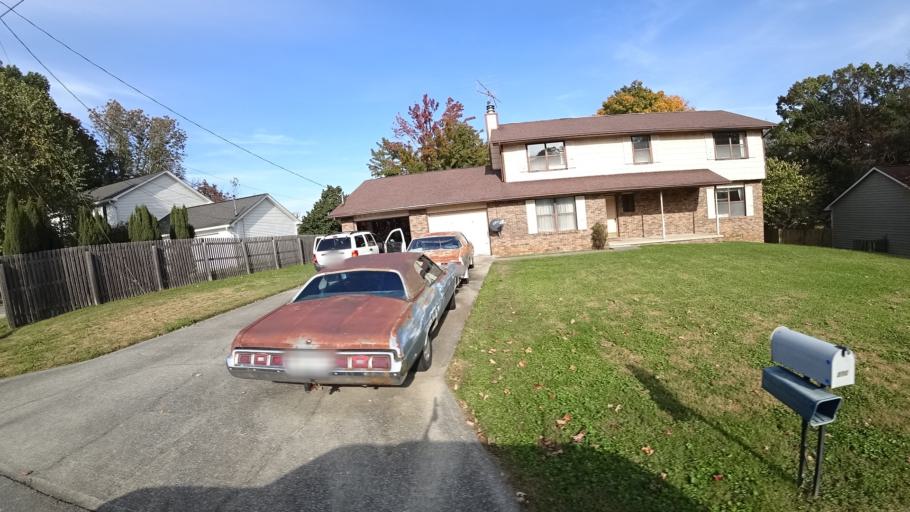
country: US
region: Tennessee
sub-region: Knox County
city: Farragut
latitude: 35.9053
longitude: -84.1614
